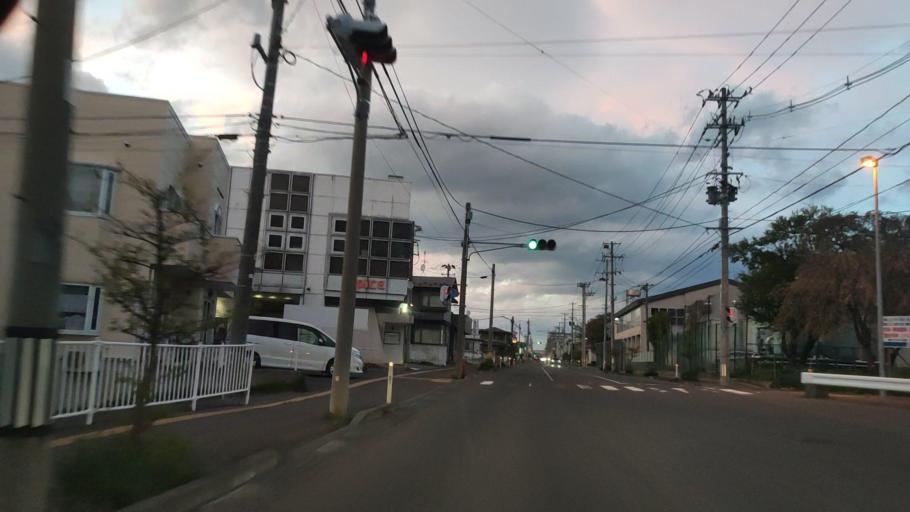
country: JP
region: Iwate
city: Morioka-shi
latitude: 39.7221
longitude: 141.1093
